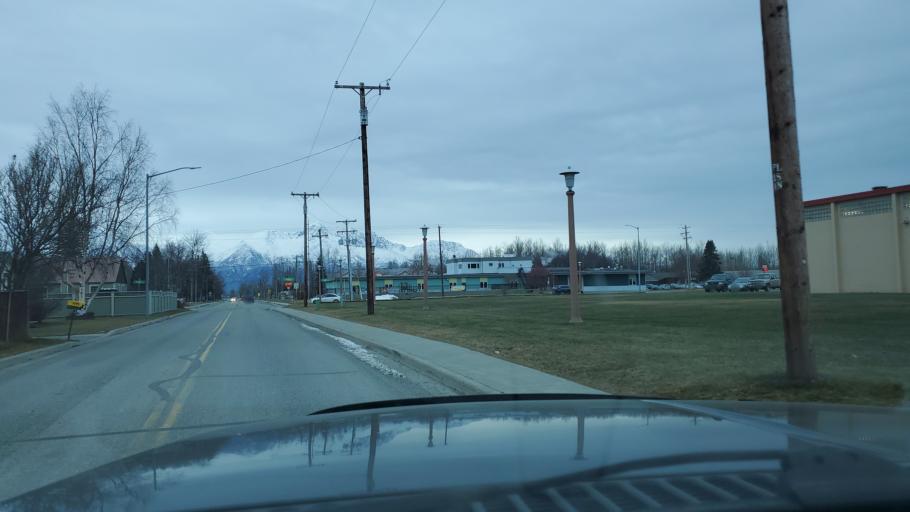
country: US
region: Alaska
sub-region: Matanuska-Susitna Borough
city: Palmer
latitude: 61.5987
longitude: -149.1108
